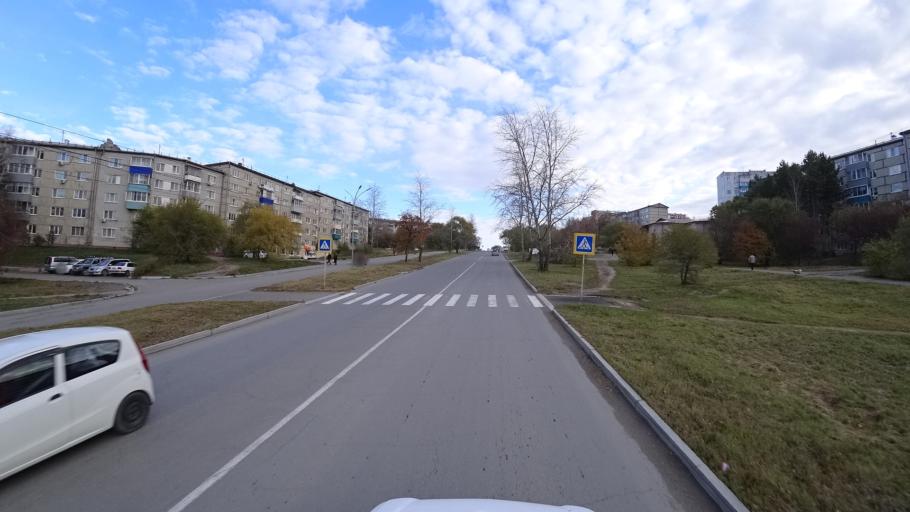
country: RU
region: Khabarovsk Krai
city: Amursk
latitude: 50.2398
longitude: 136.9120
